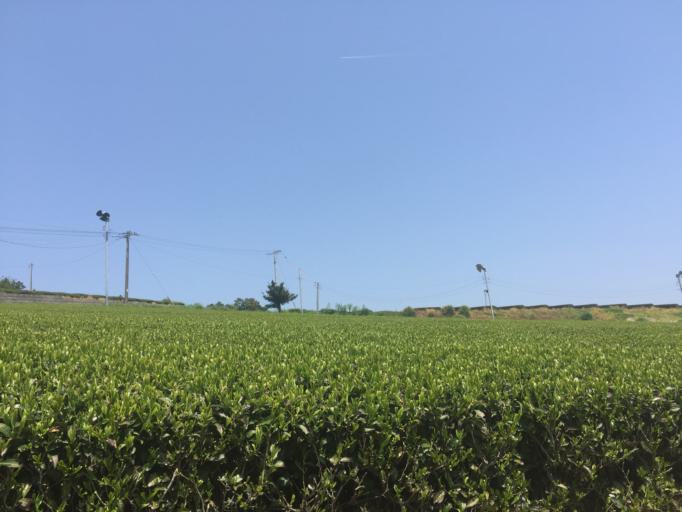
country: JP
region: Shizuoka
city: Kakegawa
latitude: 34.8106
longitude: 137.9989
